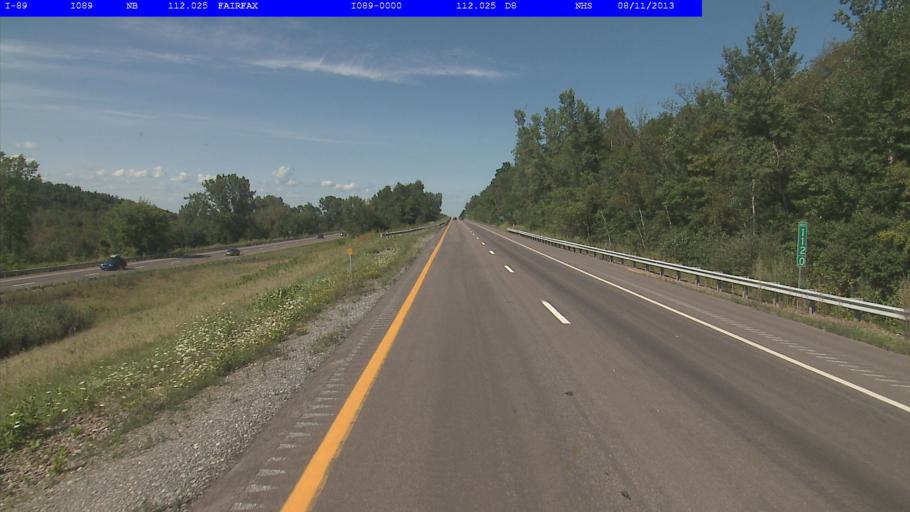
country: US
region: Vermont
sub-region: Franklin County
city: Saint Albans
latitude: 44.7704
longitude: -73.0752
